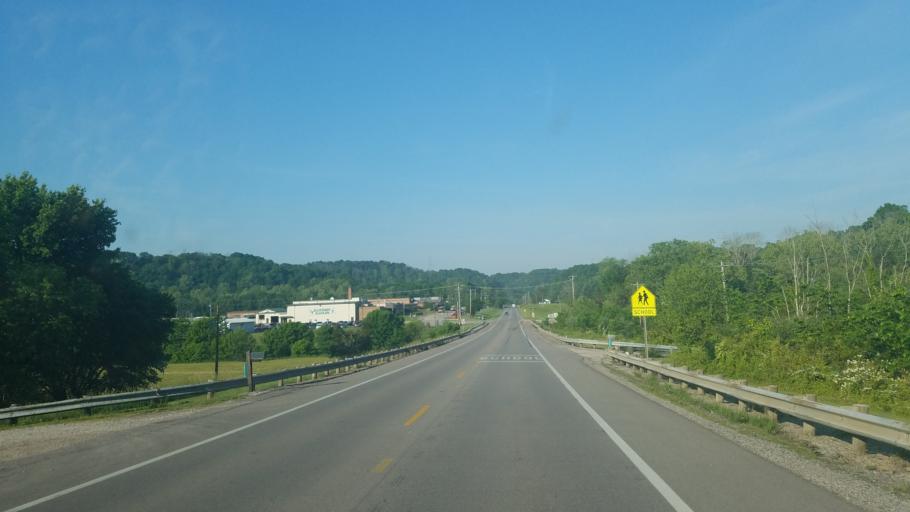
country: US
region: West Virginia
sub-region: Mason County
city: New Haven
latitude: 39.1250
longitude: -81.8806
